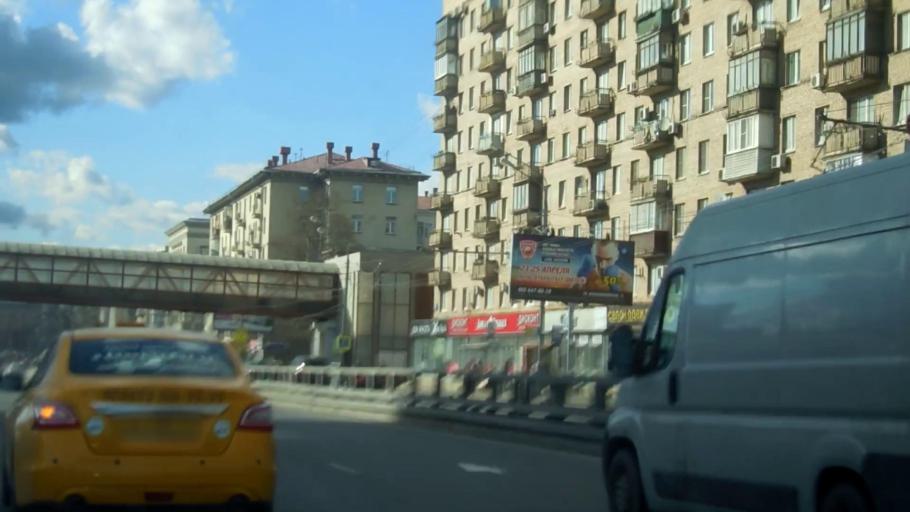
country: RU
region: Moscow
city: Sokol
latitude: 55.7976
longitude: 37.5403
